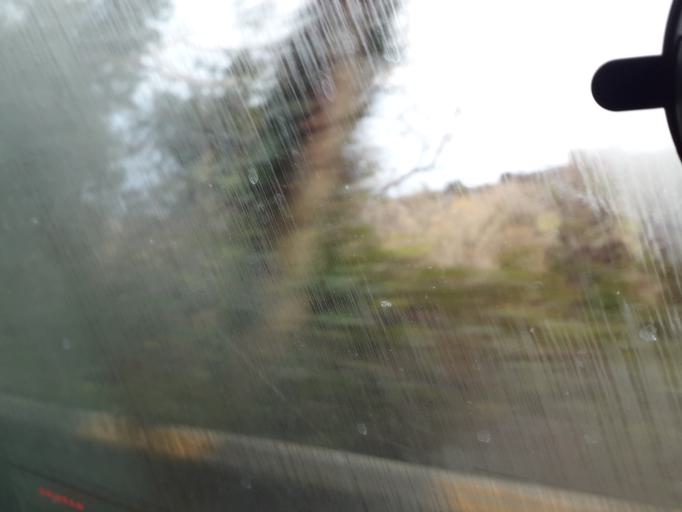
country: IE
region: Leinster
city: Ballyboden
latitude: 53.2553
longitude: -6.3018
